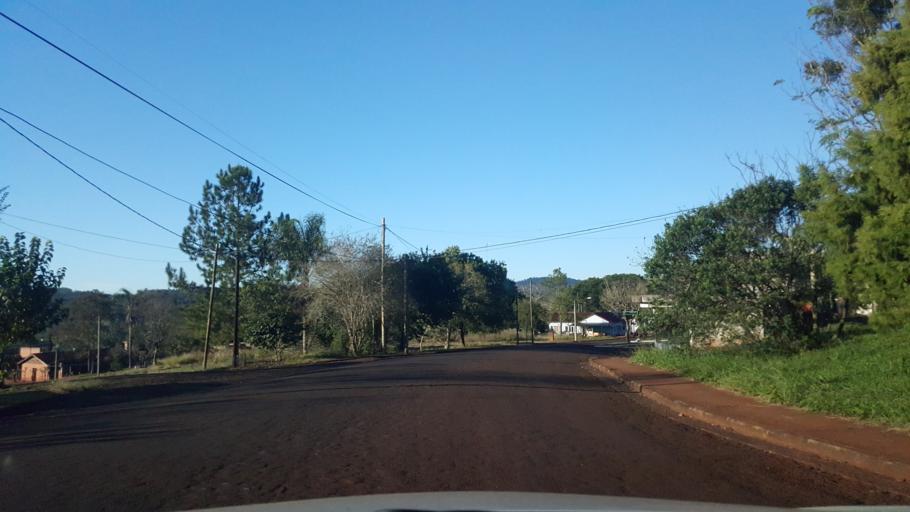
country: AR
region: Misiones
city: Capiovi
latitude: -26.9293
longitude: -55.0642
